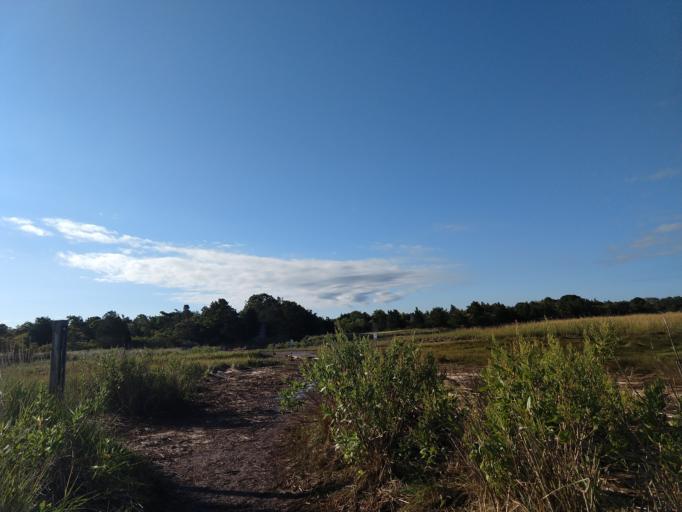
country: US
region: Massachusetts
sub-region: Barnstable County
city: North Eastham
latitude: 41.8812
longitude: -70.0015
